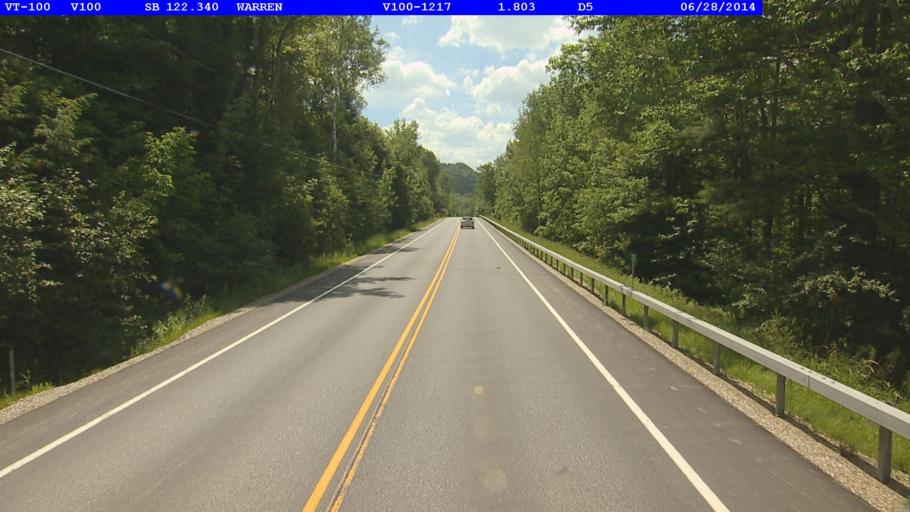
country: US
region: Vermont
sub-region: Washington County
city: Northfield
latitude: 44.0851
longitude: -72.8609
